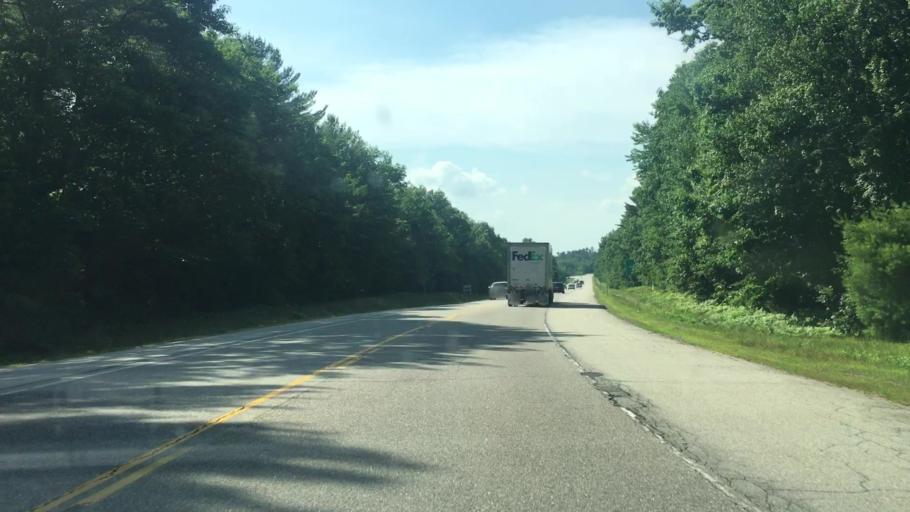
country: US
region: New Hampshire
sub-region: Strafford County
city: Rochester
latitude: 43.3253
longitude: -70.9622
